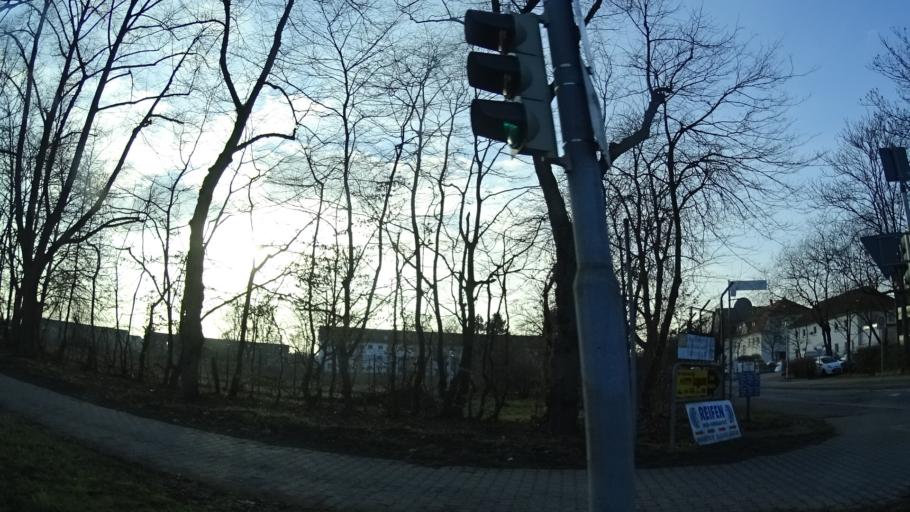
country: DE
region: Hesse
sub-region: Regierungsbezirk Darmstadt
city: Darmstadt
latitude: 49.8501
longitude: 8.6464
